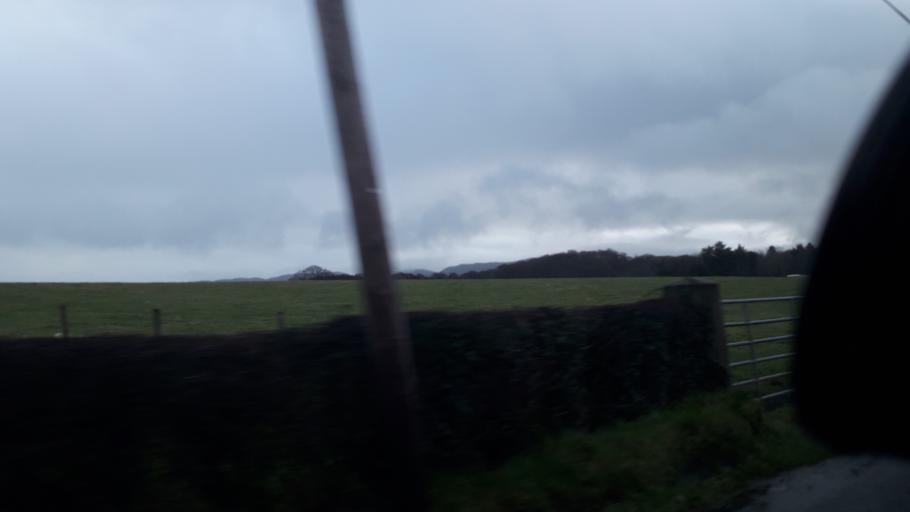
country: IE
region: Ulster
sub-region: County Donegal
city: Ramelton
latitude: 55.2029
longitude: -7.6375
